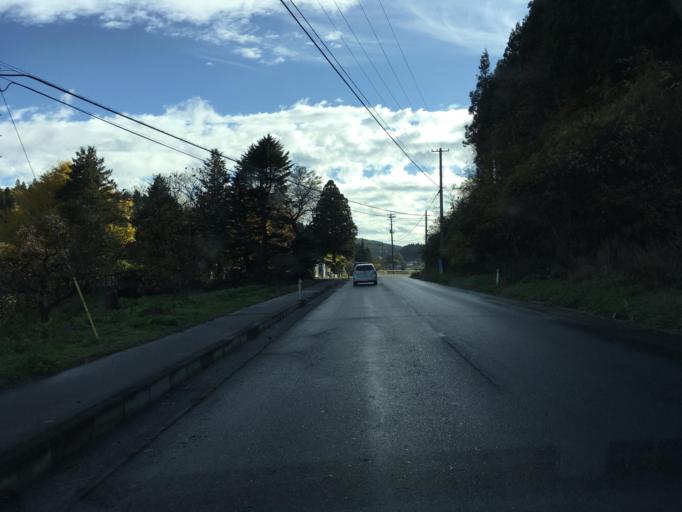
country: JP
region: Iwate
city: Ichinoseki
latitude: 38.8960
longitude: 141.4354
